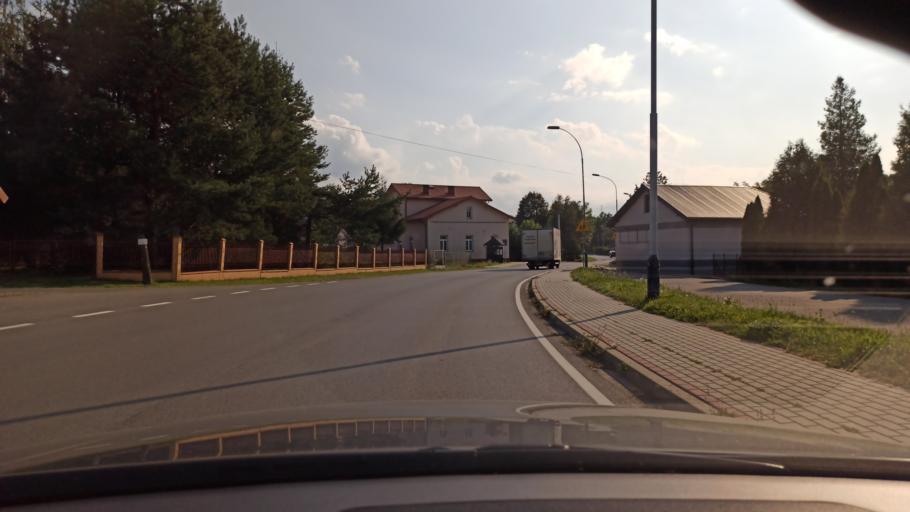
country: PL
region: Subcarpathian Voivodeship
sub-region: Powiat krosnienski
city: Iwonicz-Zdroj
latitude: 49.5979
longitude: 21.8010
